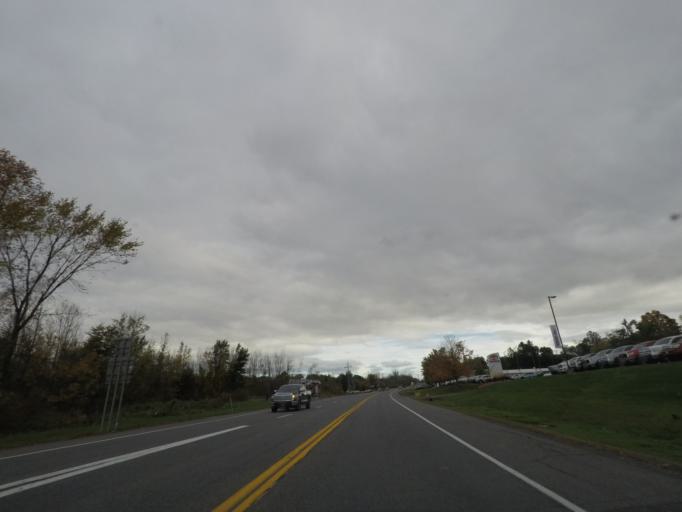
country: US
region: New York
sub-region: Saratoga County
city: Mechanicville
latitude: 42.8694
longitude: -73.7262
